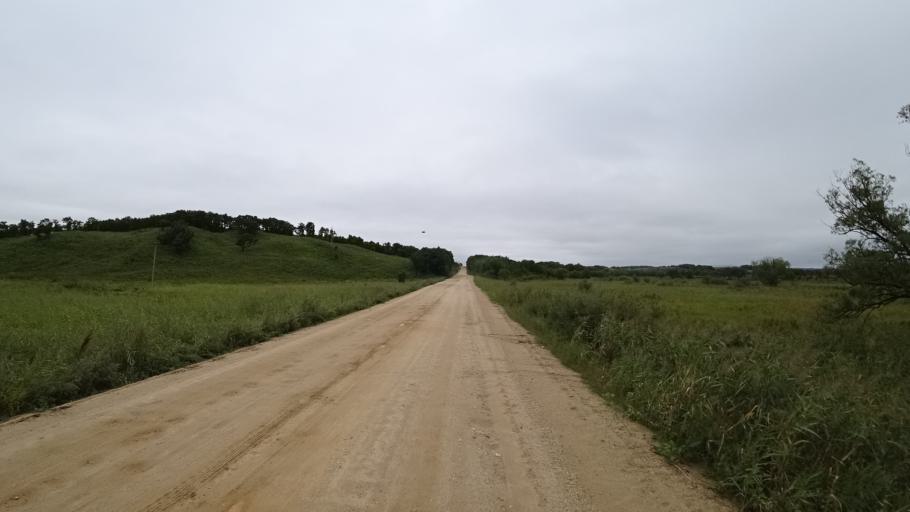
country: RU
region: Primorskiy
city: Ivanovka
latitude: 44.0708
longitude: 132.5802
